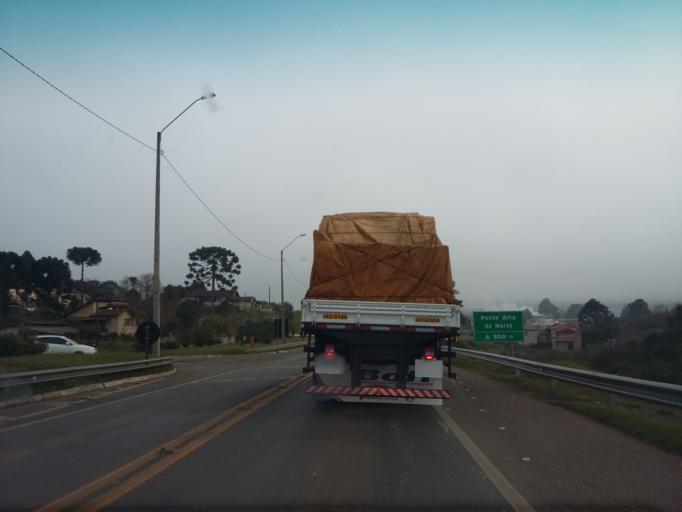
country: BR
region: Santa Catarina
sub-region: Curitibanos
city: Curitibanos
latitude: -27.1647
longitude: -50.4658
